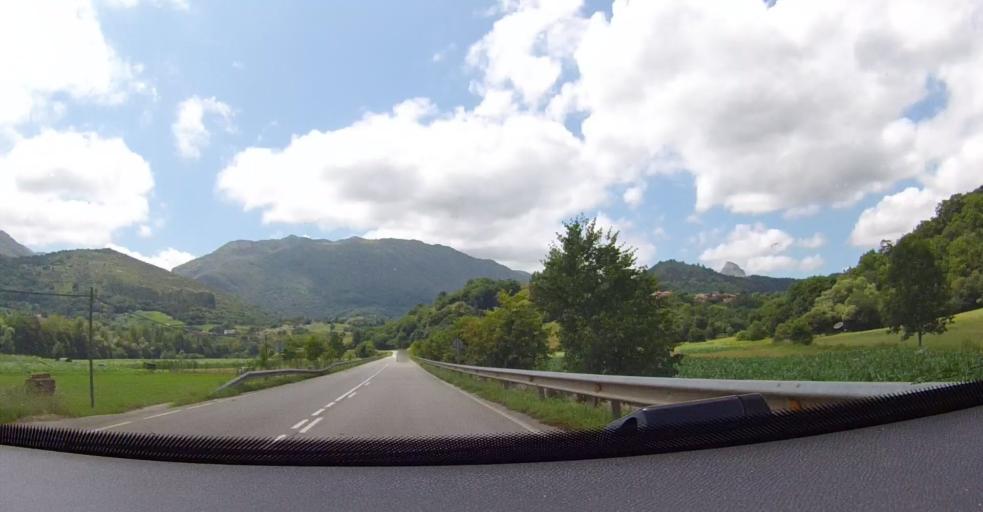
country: ES
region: Cantabria
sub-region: Provincia de Cantabria
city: Tresviso
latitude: 43.3271
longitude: -4.5915
